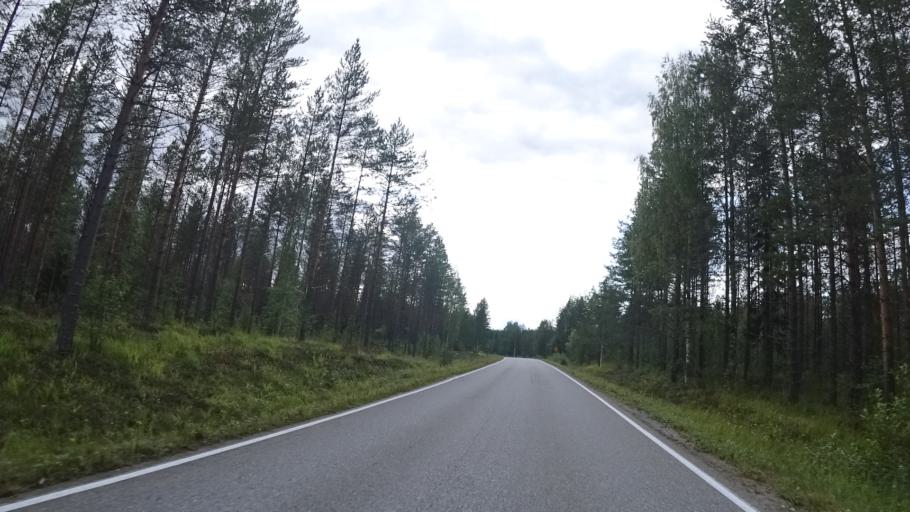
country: FI
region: North Karelia
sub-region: Joensuu
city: Ilomantsi
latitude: 62.4359
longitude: 31.0623
